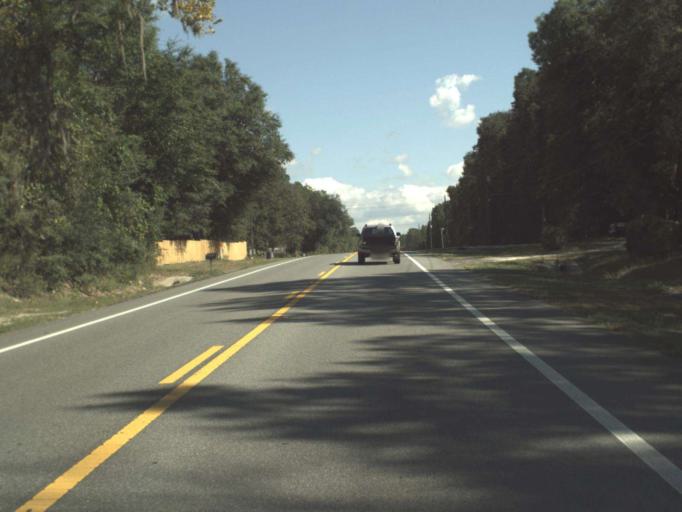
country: US
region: Florida
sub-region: Walton County
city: Freeport
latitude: 30.4872
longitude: -86.1129
